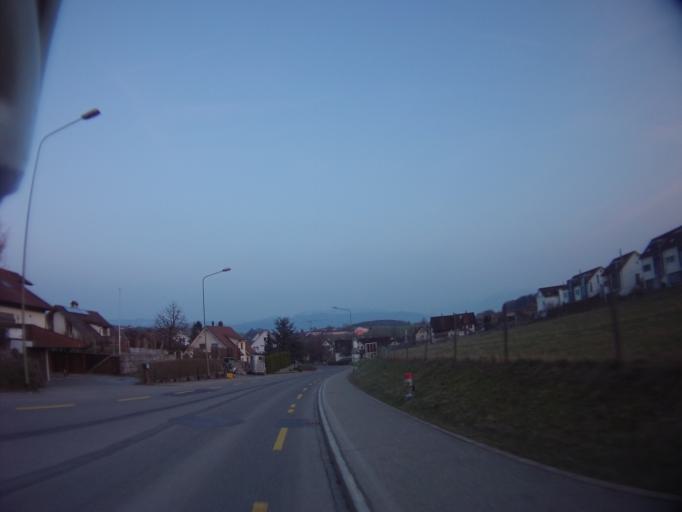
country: CH
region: Zurich
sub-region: Bezirk Affoltern
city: Knonau
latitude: 47.2257
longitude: 8.4584
